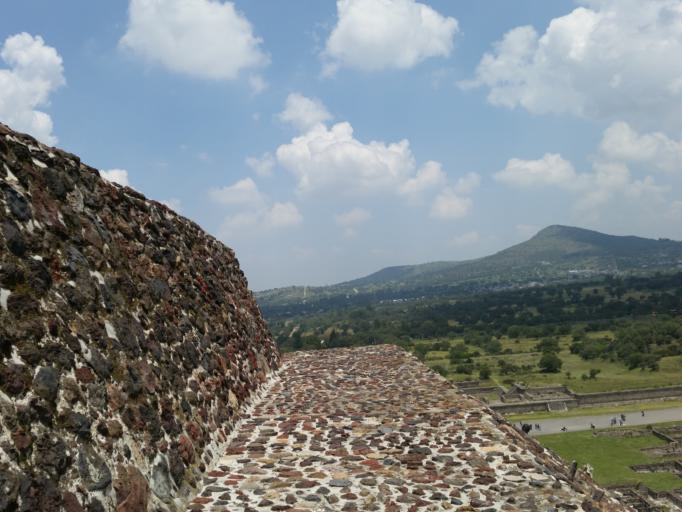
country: MX
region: Morelos
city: San Martin de las Piramides
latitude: 19.6929
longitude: -98.8437
